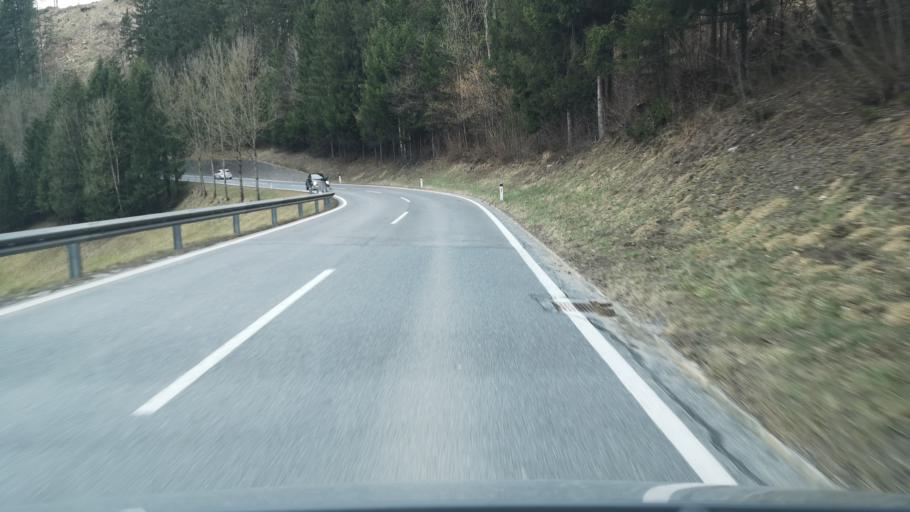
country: AT
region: Styria
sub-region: Politischer Bezirk Weiz
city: Birkfeld
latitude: 47.3367
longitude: 15.6963
